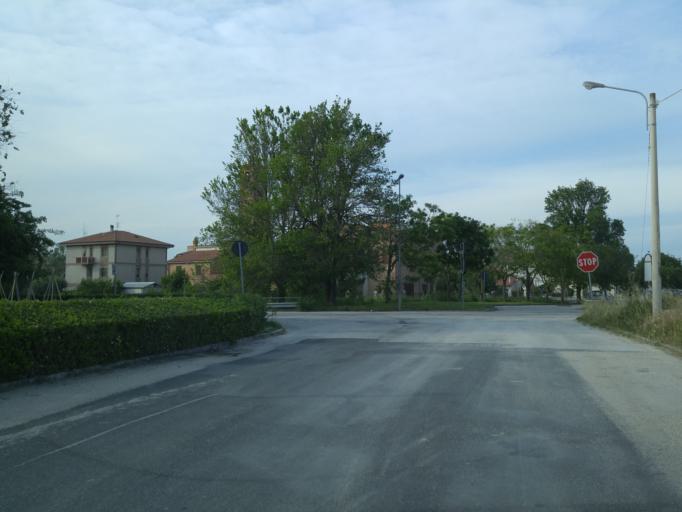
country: IT
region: The Marches
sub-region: Provincia di Ancona
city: Senigallia
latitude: 43.6982
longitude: 13.2464
